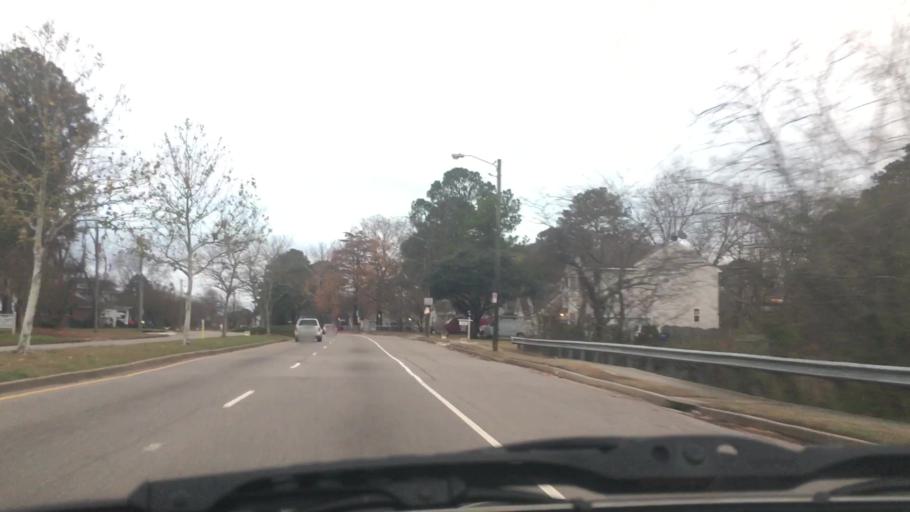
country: US
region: Virginia
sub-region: City of Norfolk
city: Norfolk
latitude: 36.8840
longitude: -76.2459
